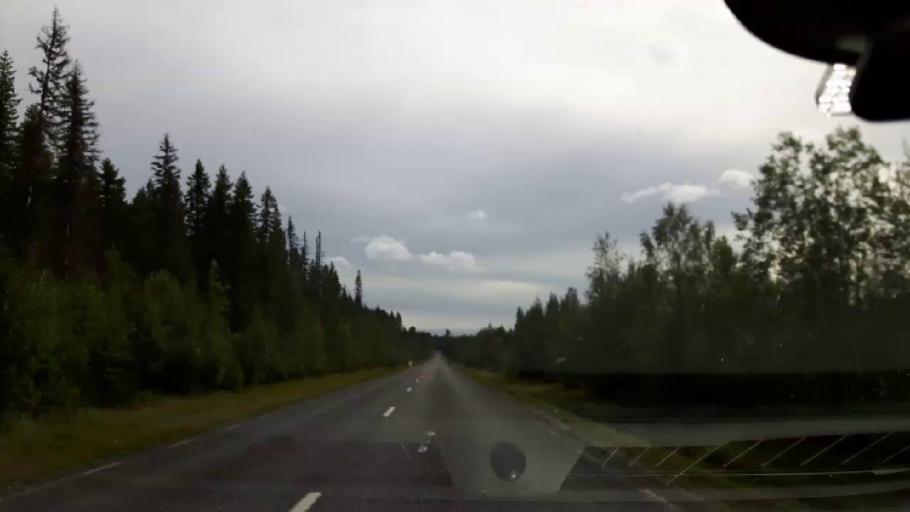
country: SE
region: Jaemtland
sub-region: Ragunda Kommun
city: Hammarstrand
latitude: 63.1215
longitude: 15.8987
